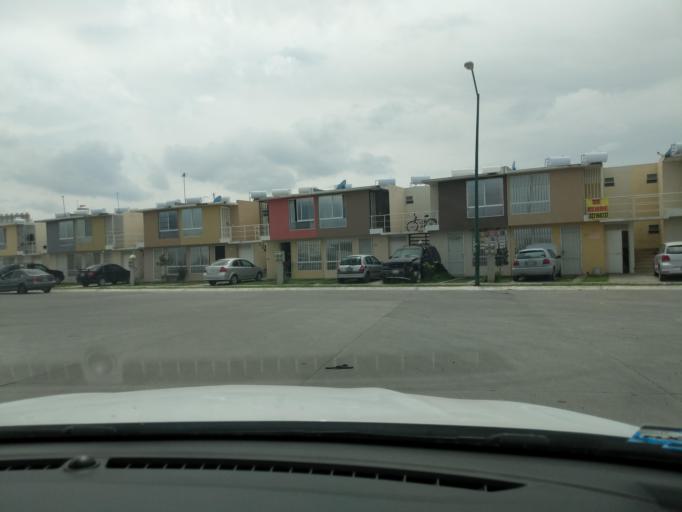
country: MX
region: Jalisco
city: Tesistan
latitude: 20.7860
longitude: -103.4893
